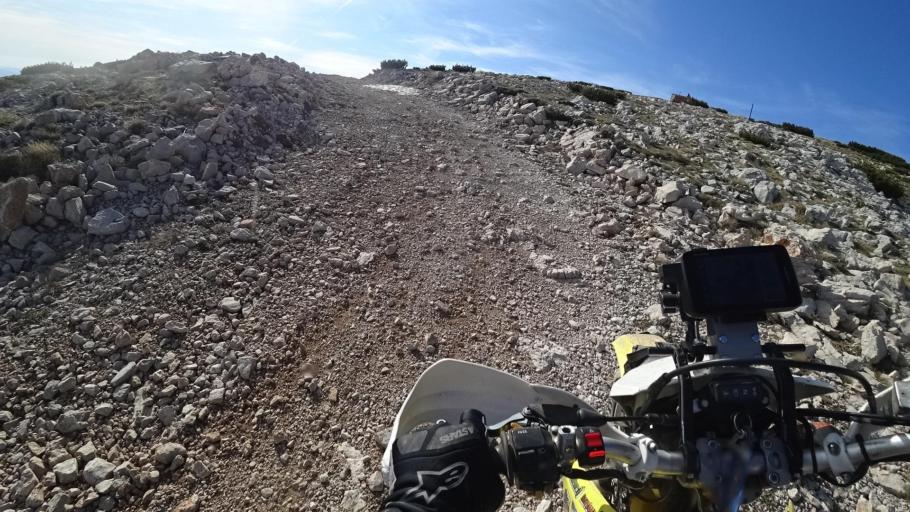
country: BA
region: Federation of Bosnia and Herzegovina
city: Kocerin
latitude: 43.5985
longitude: 17.5452
